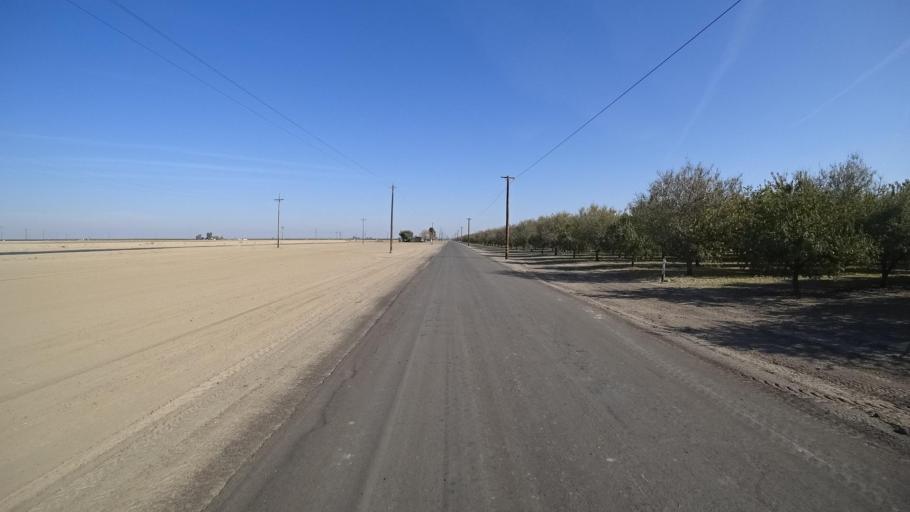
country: US
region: California
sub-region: Kern County
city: Wasco
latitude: 35.6597
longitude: -119.3975
